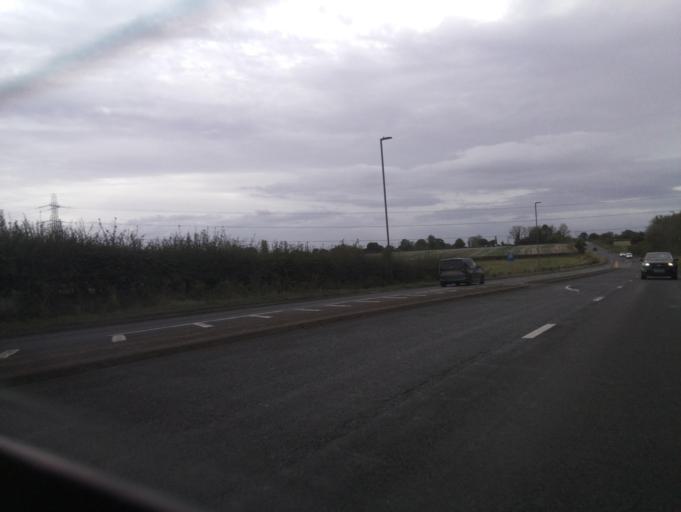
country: GB
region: England
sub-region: South Gloucestershire
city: Thornbury
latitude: 51.5950
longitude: -2.5115
